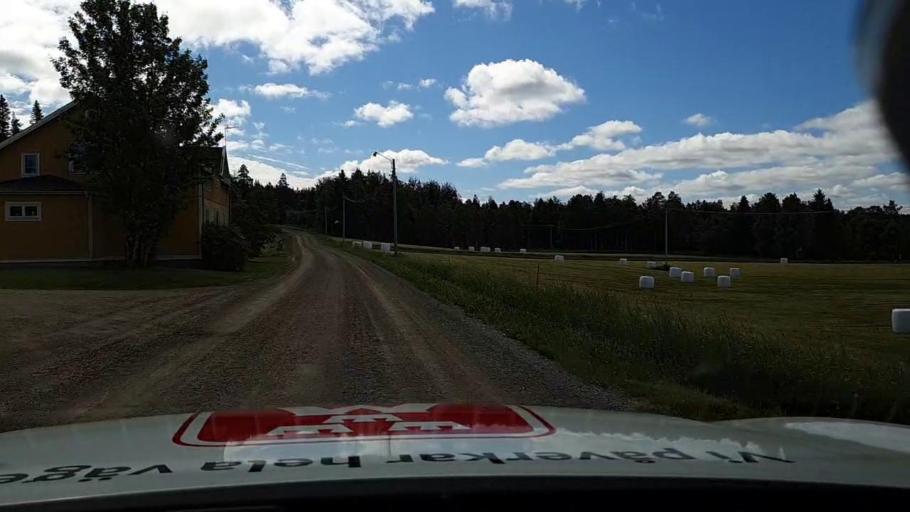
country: SE
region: Jaemtland
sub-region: Braecke Kommun
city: Braecke
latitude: 62.7761
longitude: 15.4789
